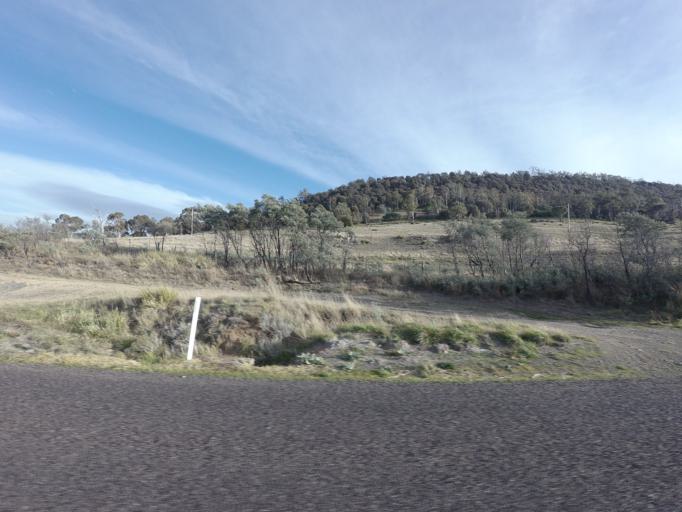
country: AU
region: Tasmania
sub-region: Brighton
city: Bridgewater
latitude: -42.4084
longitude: 147.1163
